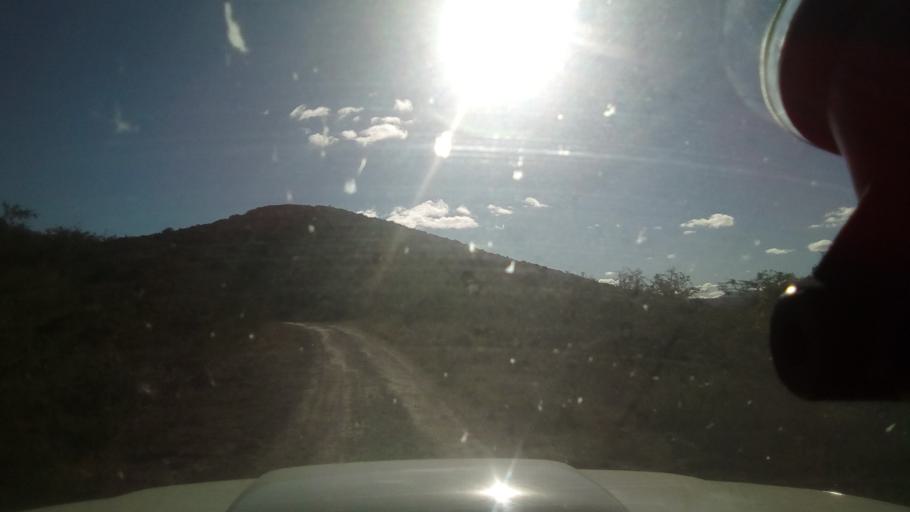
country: ZA
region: Eastern Cape
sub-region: Buffalo City Metropolitan Municipality
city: Bhisho
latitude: -32.7414
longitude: 27.3496
